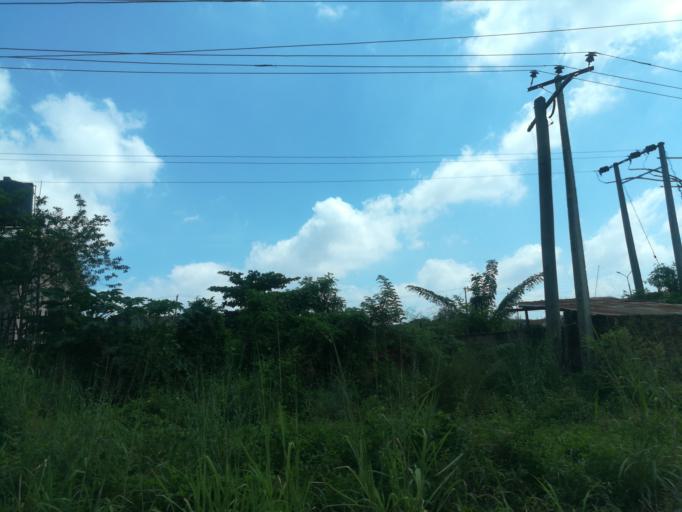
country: NG
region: Oyo
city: Ibadan
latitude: 7.3536
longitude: 3.8623
